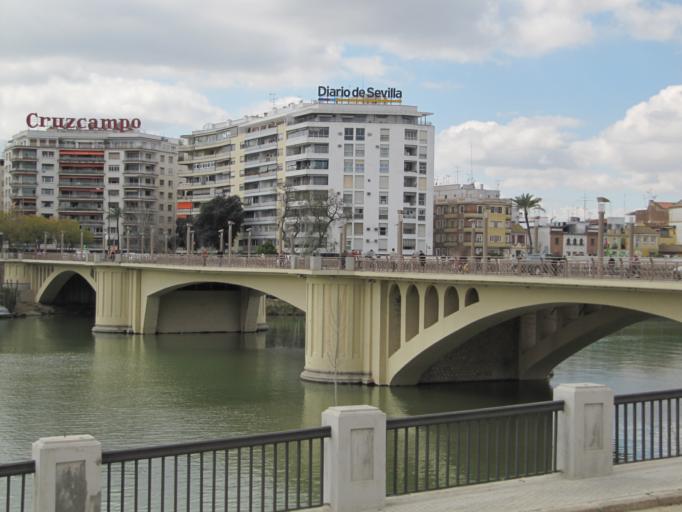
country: ES
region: Andalusia
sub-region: Provincia de Sevilla
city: Sevilla
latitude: 37.3809
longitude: -5.9953
